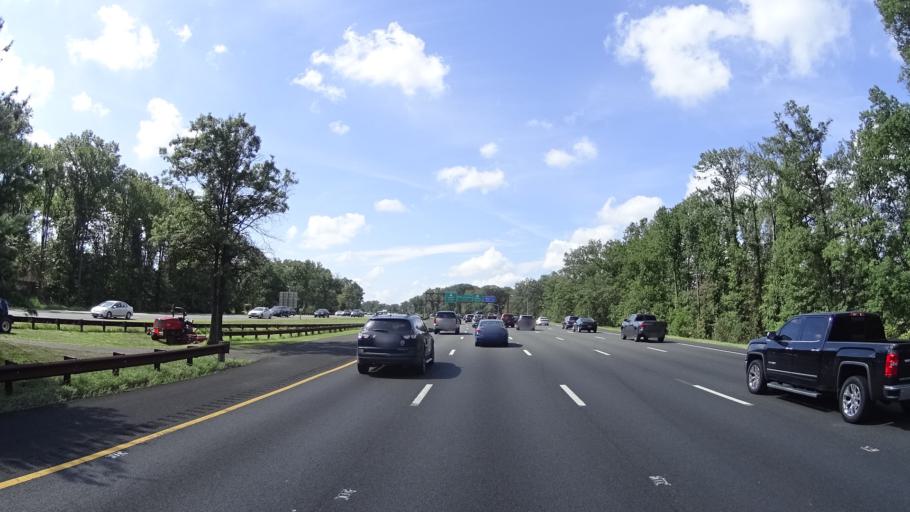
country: US
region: New Jersey
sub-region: Middlesex County
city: Iselin
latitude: 40.5851
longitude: -74.3290
